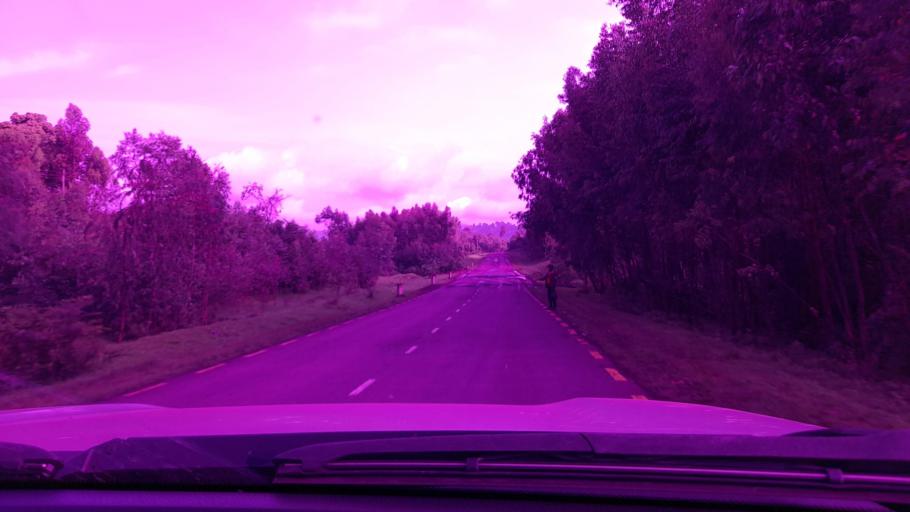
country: ET
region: Oromiya
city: Bedele
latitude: 8.1983
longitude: 36.4434
